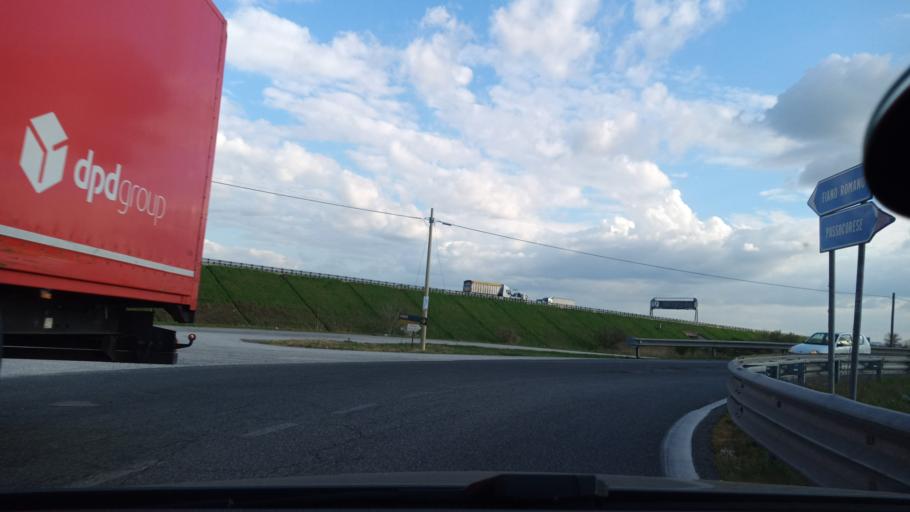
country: IT
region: Latium
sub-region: Citta metropolitana di Roma Capitale
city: Fiano Romano
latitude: 42.1479
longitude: 12.6224
